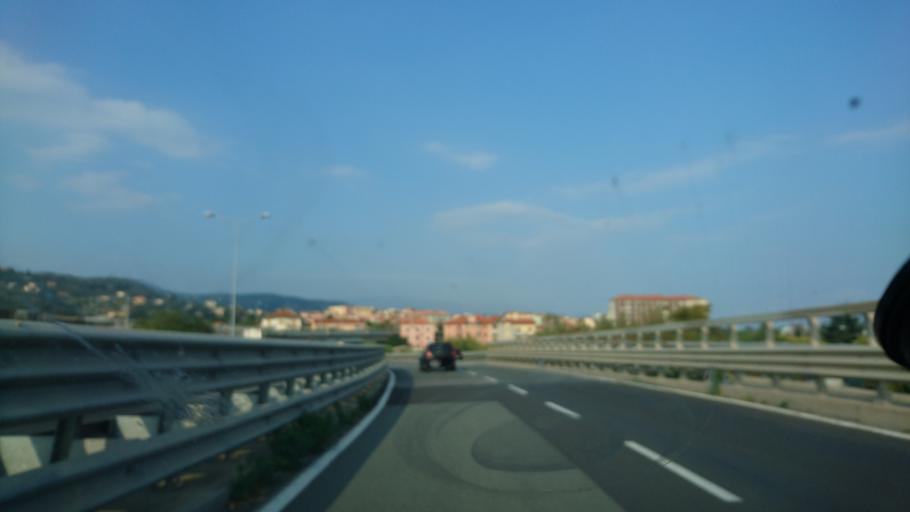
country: IT
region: Liguria
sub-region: Provincia di Savona
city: Valleggia
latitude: 44.2801
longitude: 8.4394
